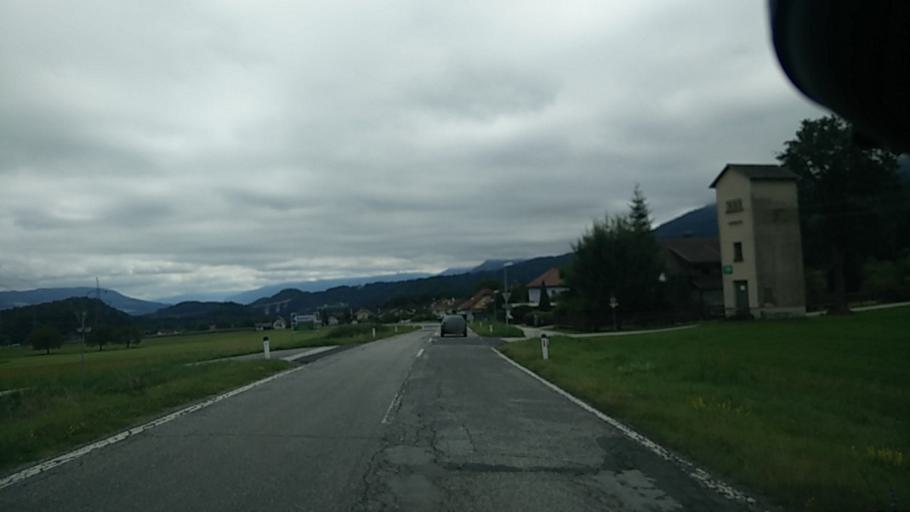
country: AT
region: Carinthia
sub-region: Politischer Bezirk Villach Land
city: Rosegg
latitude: 46.5557
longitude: 13.9737
